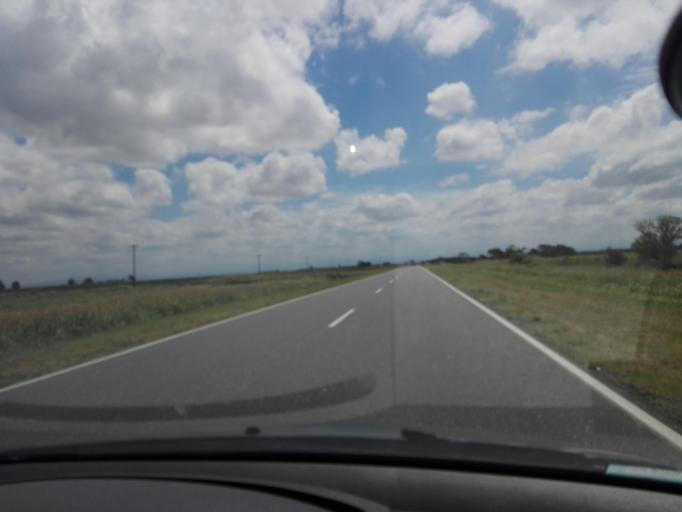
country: AR
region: Cordoba
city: Toledo
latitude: -31.6462
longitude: -64.0431
